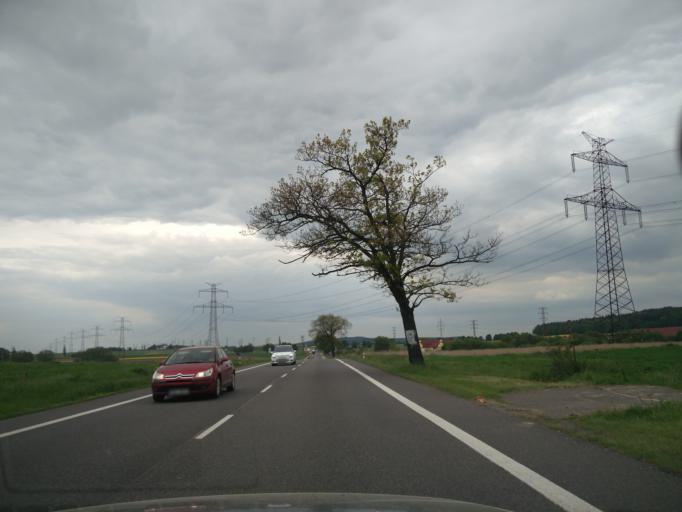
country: CZ
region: Jihocesky
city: Mirovice
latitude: 49.5299
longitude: 14.0767
